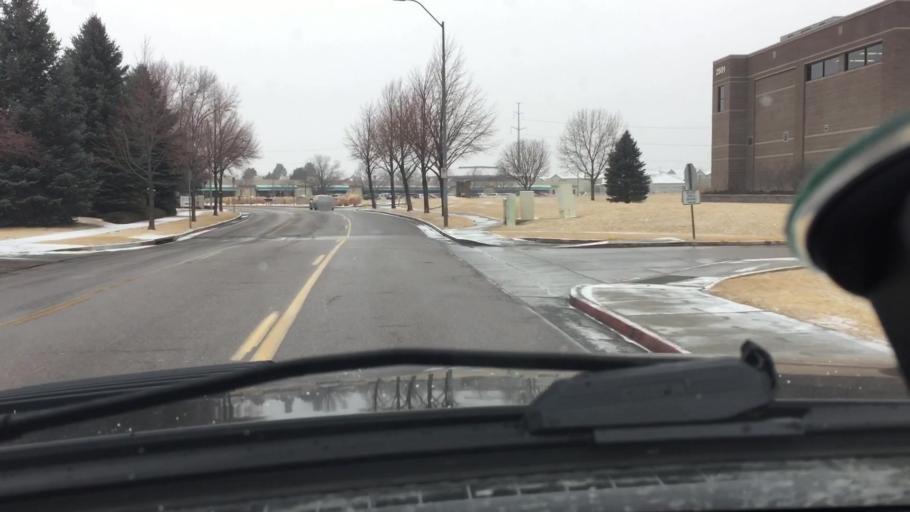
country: US
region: Colorado
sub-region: Larimer County
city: Fort Collins
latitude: 40.5637
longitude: -105.0321
